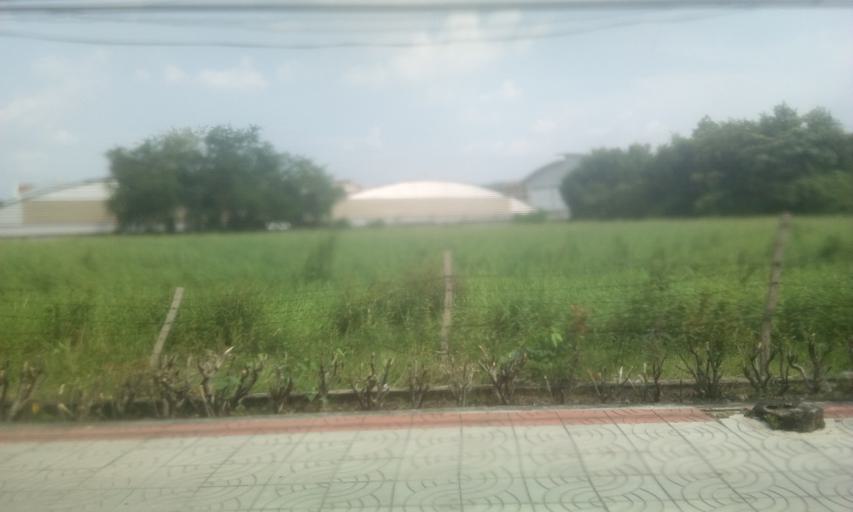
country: TH
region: Bangkok
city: Sai Mai
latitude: 13.9476
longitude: 100.6173
